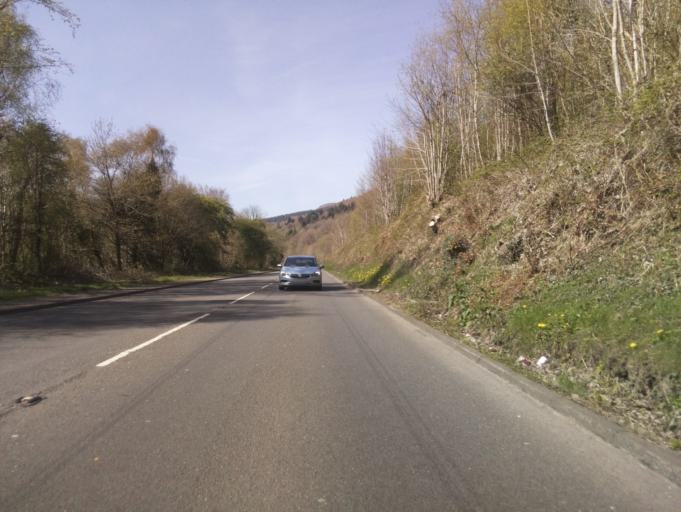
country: GB
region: Wales
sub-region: Merthyr Tydfil County Borough
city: Treharris
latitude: 51.6591
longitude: -3.3380
